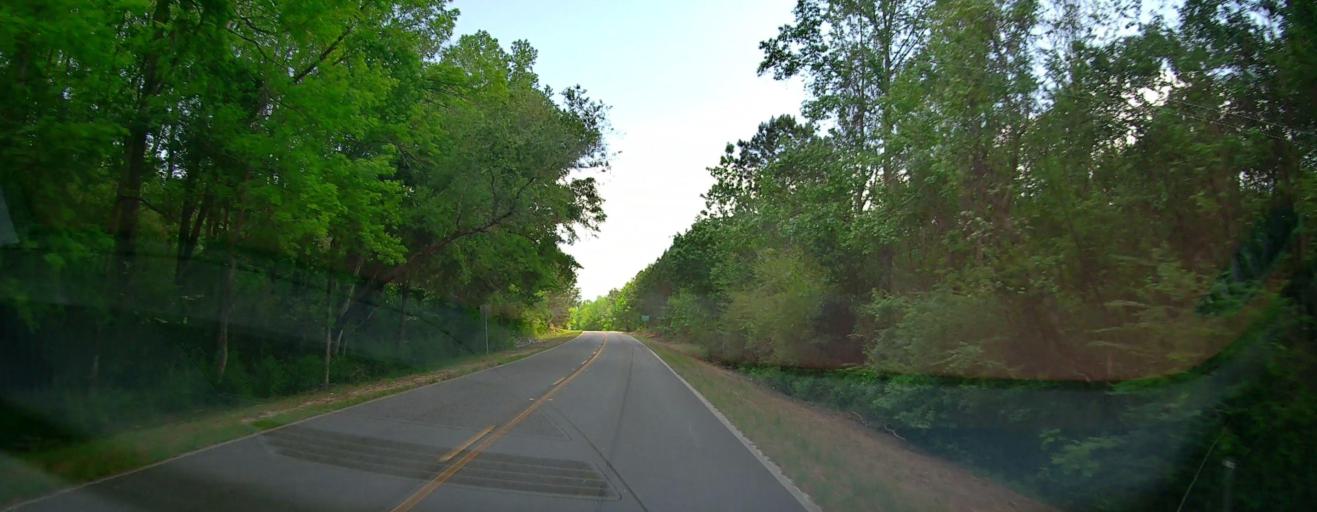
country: US
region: Georgia
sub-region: Treutlen County
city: Soperton
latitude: 32.5175
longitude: -82.6618
